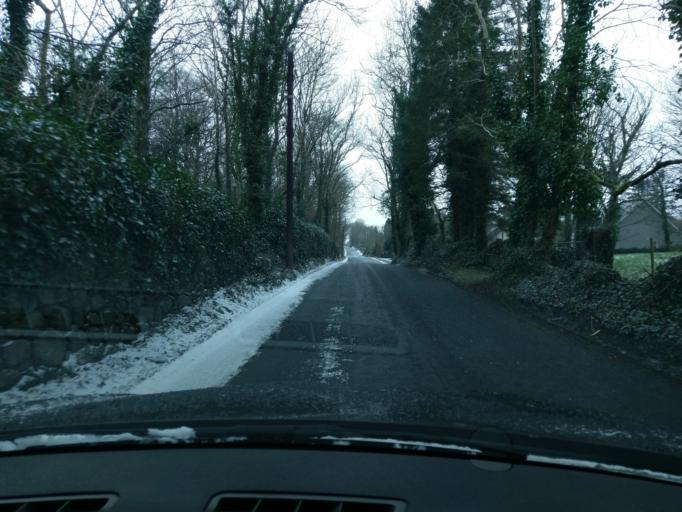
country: IE
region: Connaught
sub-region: County Galway
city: Oranmore
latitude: 53.2429
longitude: -8.8581
